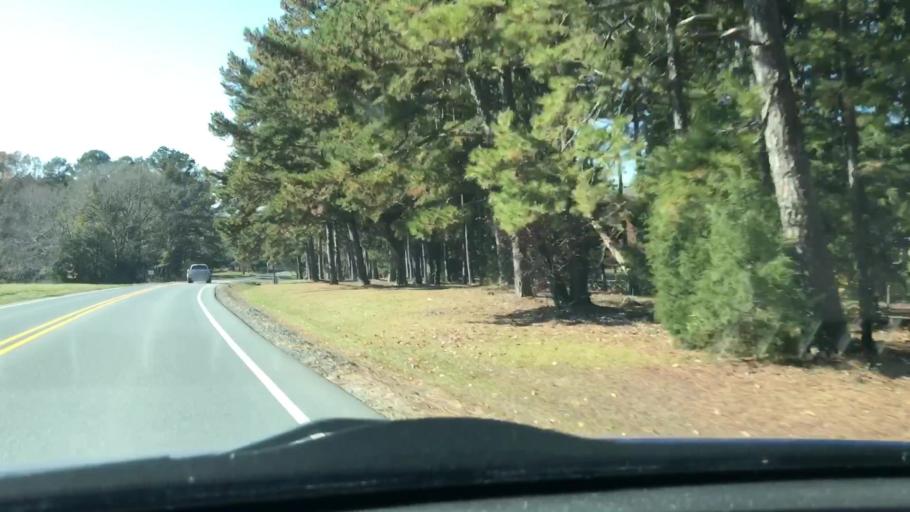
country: US
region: North Carolina
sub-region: Randolph County
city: Asheboro
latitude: 35.6771
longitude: -79.8750
